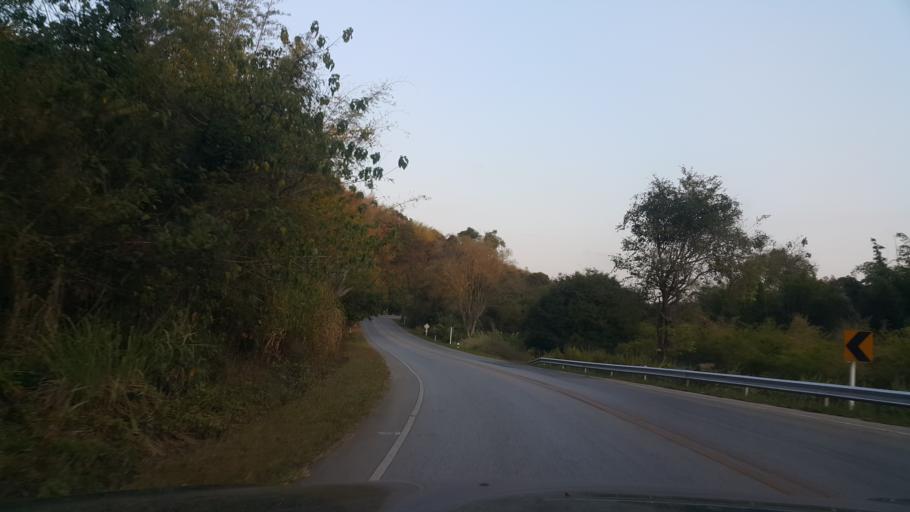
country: TH
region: Loei
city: Loei
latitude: 17.4705
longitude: 101.5836
